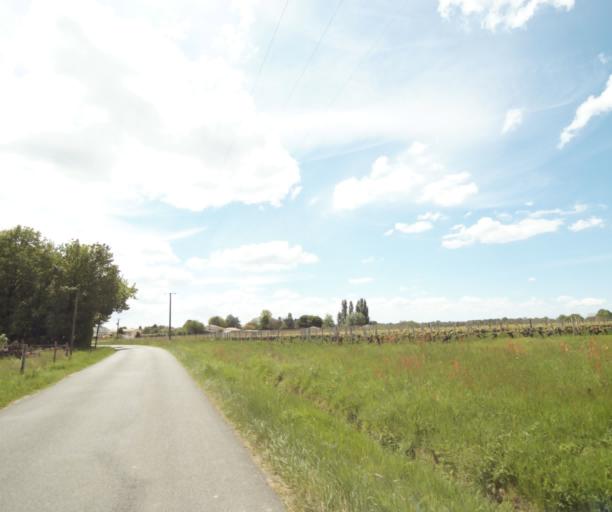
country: FR
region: Poitou-Charentes
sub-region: Departement de la Charente-Maritime
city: Burie
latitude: 45.7509
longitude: -0.4457
